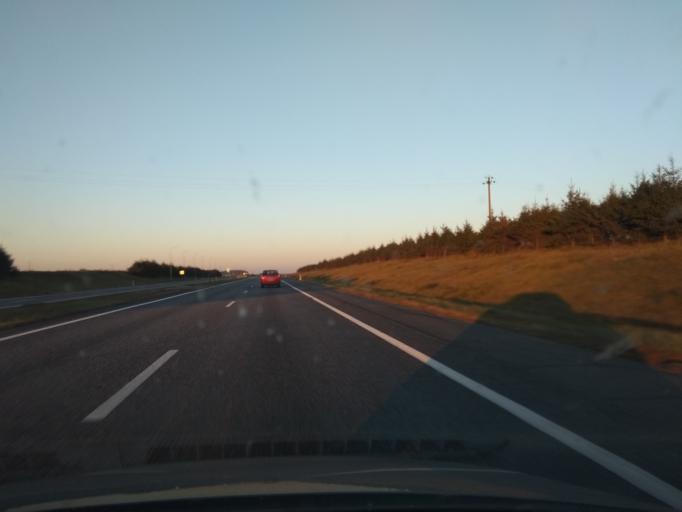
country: BY
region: Minsk
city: Haradzyeya
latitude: 53.3530
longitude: 26.4622
